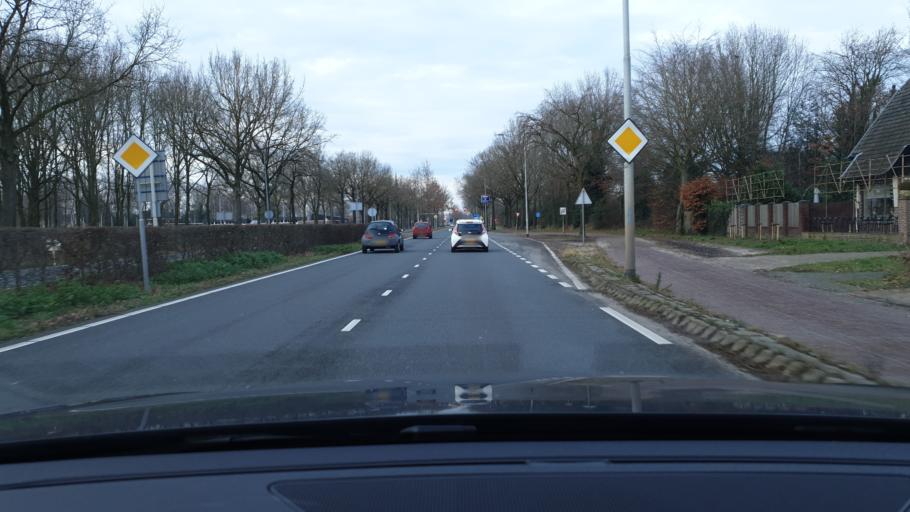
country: NL
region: North Brabant
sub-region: Gemeente Eindhoven
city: Meerhoven
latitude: 51.4808
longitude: 5.4357
